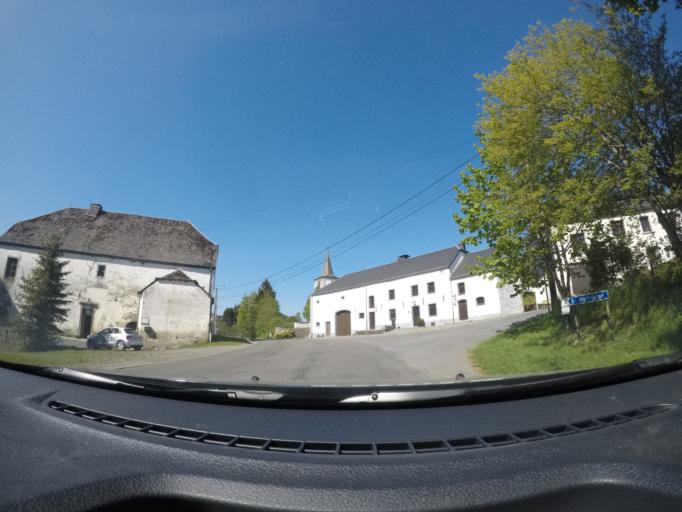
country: BE
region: Wallonia
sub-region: Province du Luxembourg
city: Fauvillers
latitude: 49.8534
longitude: 5.6988
